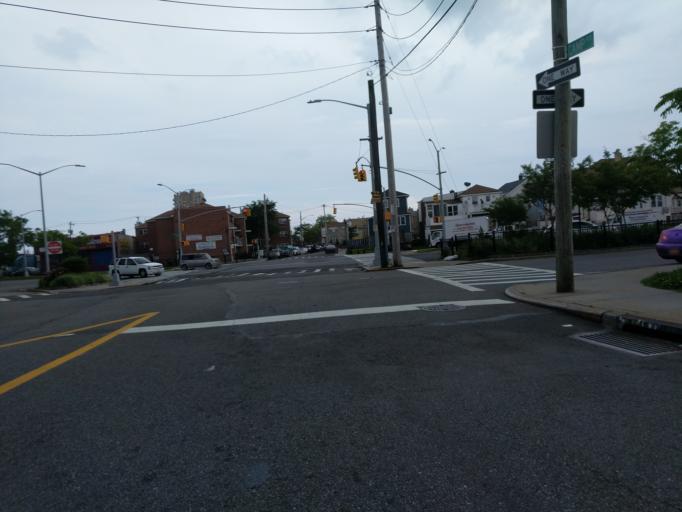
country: US
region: New York
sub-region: Nassau County
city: Inwood
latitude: 40.5964
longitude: -73.7597
